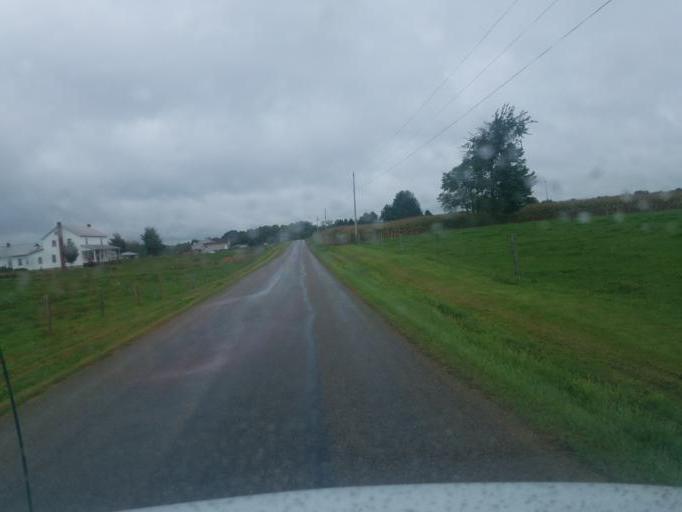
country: US
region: Ohio
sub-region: Wayne County
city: West Salem
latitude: 40.9257
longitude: -82.1187
